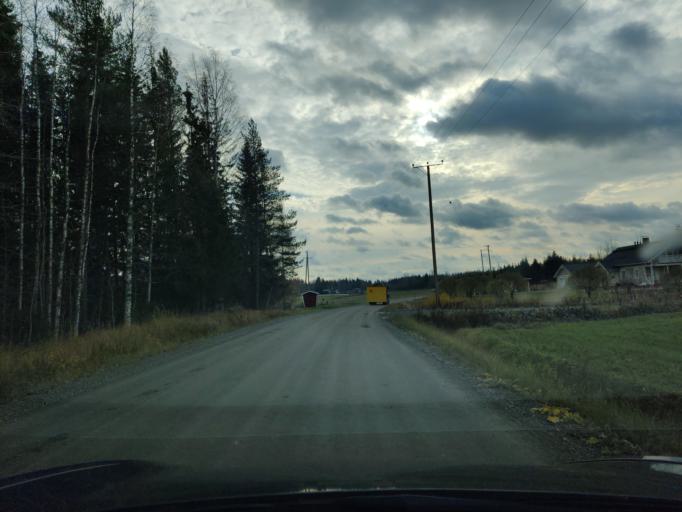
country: FI
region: Northern Savo
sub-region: Kuopio
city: Siilinjaervi
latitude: 63.1078
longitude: 27.5561
